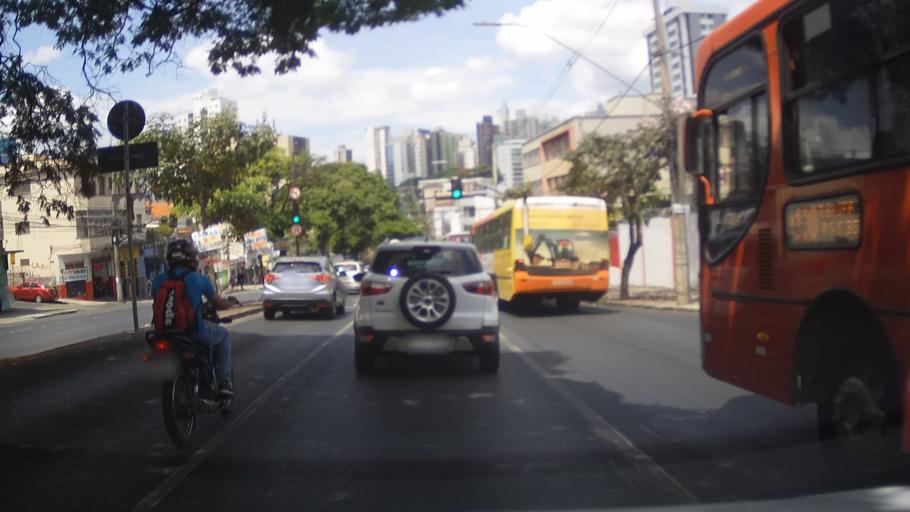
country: BR
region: Minas Gerais
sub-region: Belo Horizonte
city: Belo Horizonte
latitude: -19.9305
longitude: -43.9619
